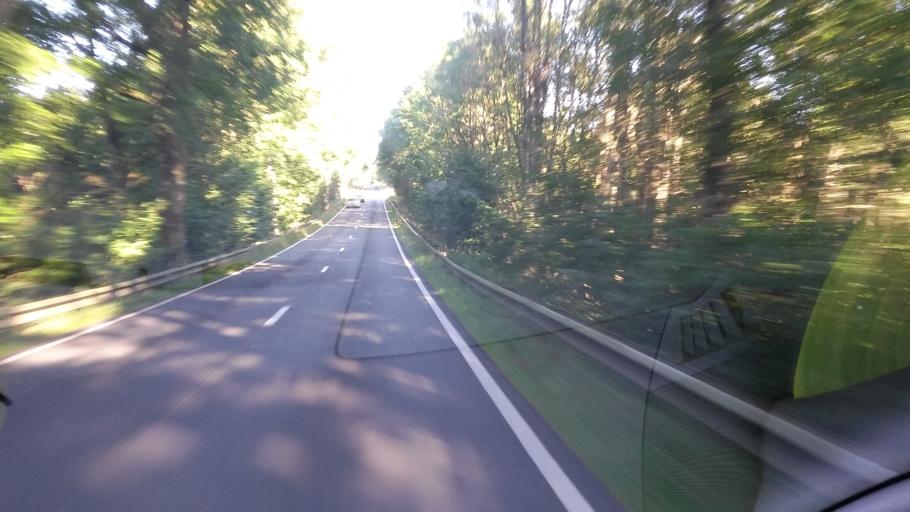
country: BE
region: Wallonia
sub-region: Province du Luxembourg
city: Leglise
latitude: 49.8114
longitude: 5.5066
